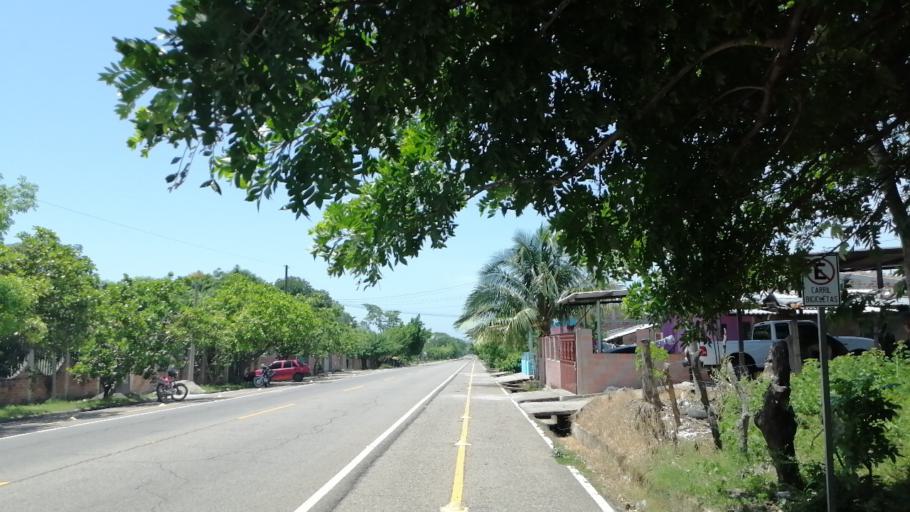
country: SV
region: Chalatenango
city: Nueva Concepcion
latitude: 14.1392
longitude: -89.2944
